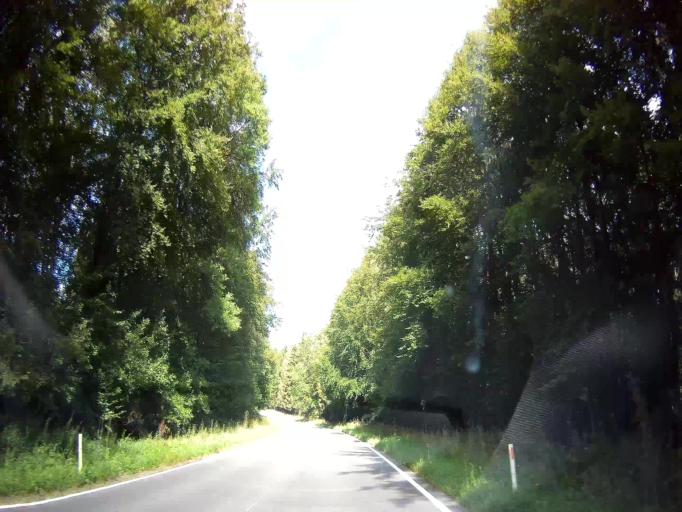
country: BE
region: Wallonia
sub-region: Province du Luxembourg
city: Bastogne
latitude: 50.0330
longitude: 5.6975
